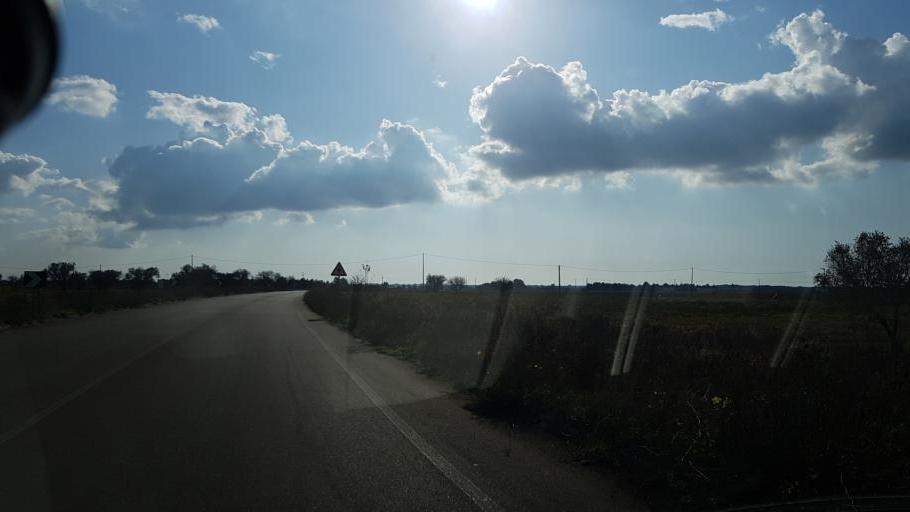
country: IT
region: Apulia
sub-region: Provincia di Lecce
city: Veglie
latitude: 40.3320
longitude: 17.9823
